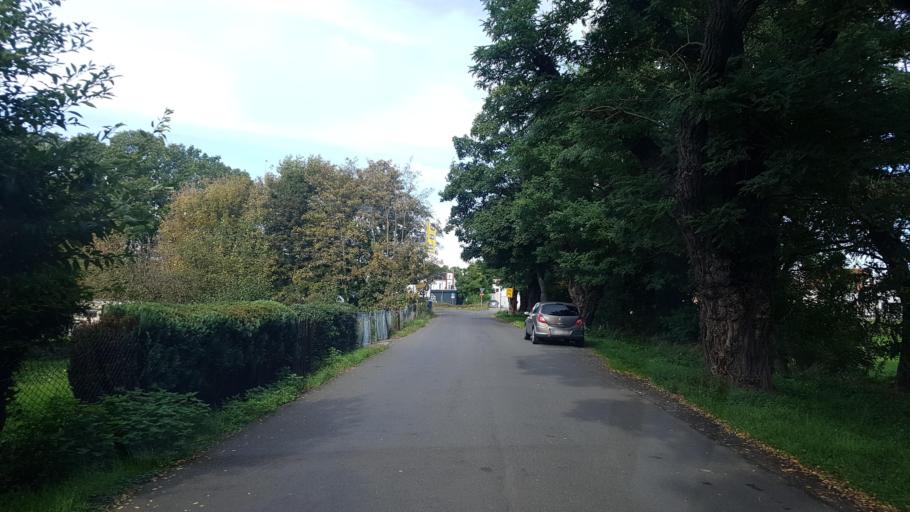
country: DE
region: Saxony
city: Pegau
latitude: 51.1638
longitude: 12.2653
